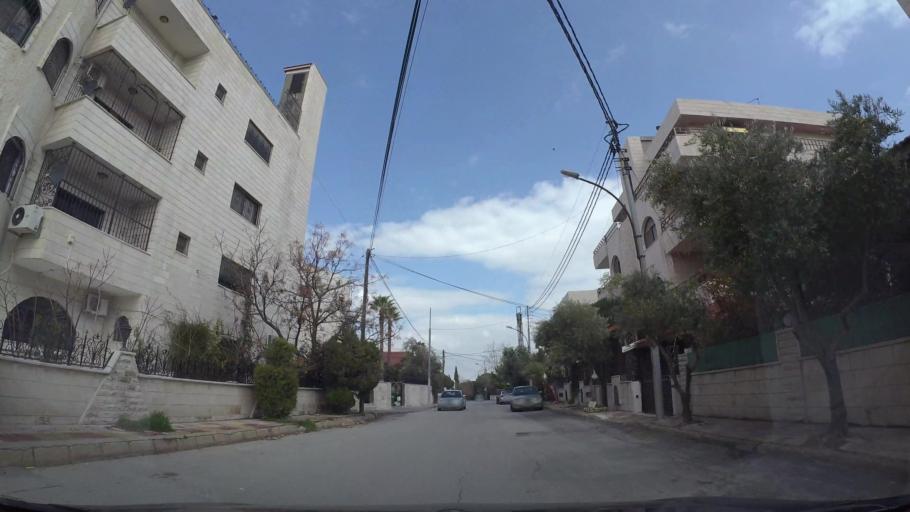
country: JO
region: Amman
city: Amman
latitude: 31.9820
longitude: 35.8991
